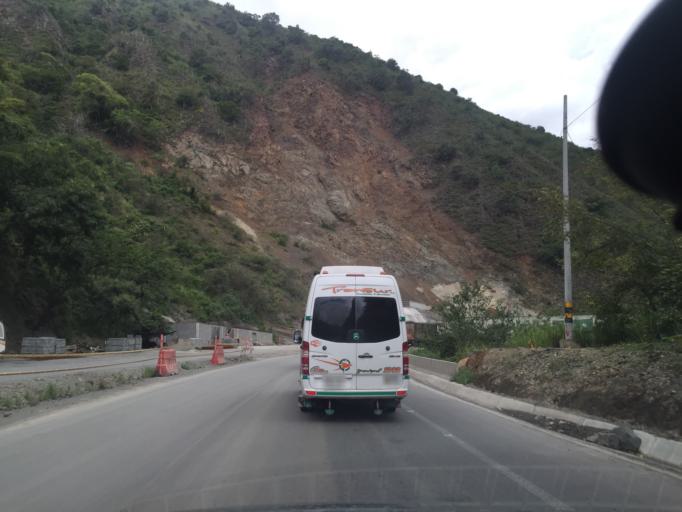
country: CO
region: Valle del Cauca
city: Dagua
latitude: 3.7763
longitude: -76.7002
